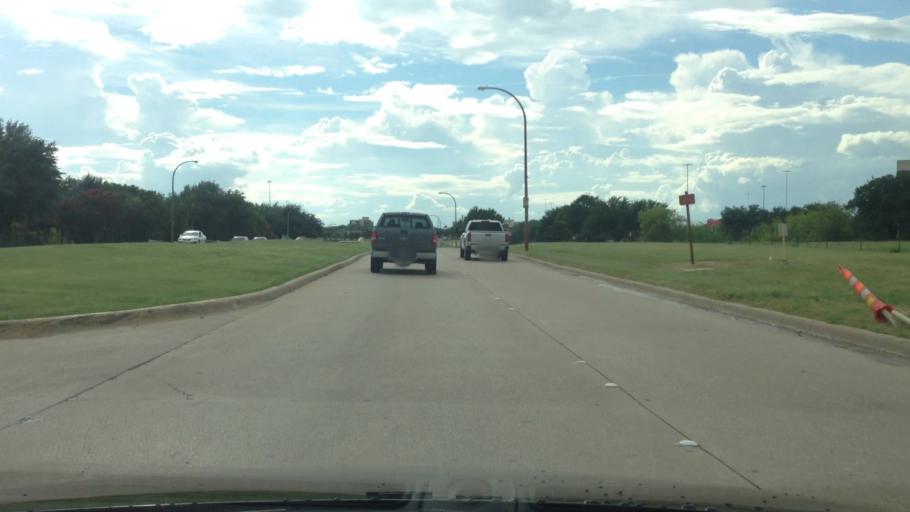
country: US
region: Texas
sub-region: Tarrant County
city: Haltom City
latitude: 32.8243
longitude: -97.3045
